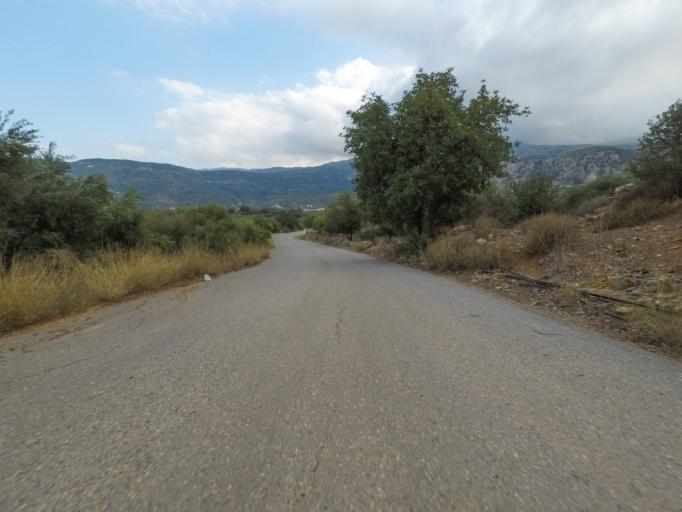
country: GR
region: Crete
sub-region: Nomos Lasithiou
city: Kritsa
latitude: 35.1660
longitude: 25.6550
